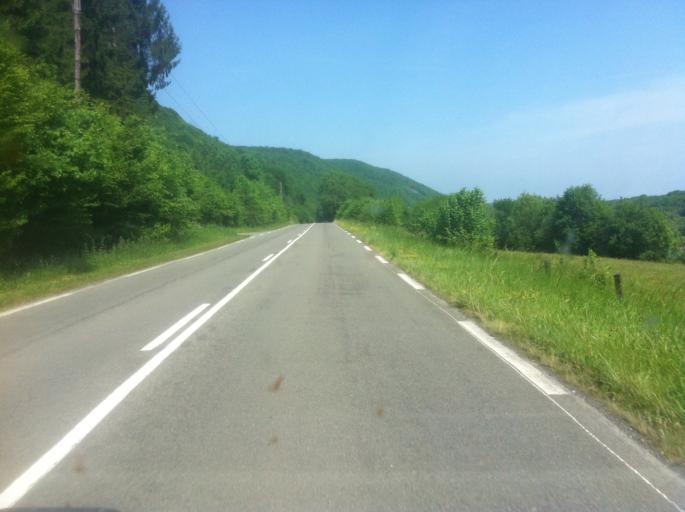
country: FR
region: Champagne-Ardenne
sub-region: Departement des Ardennes
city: Vireux-Molhain
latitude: 50.0437
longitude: 4.7225
